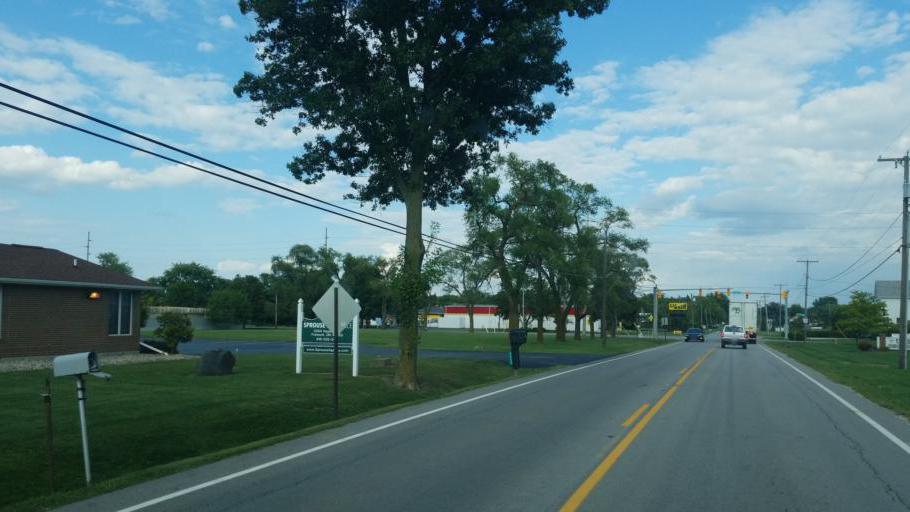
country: US
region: Ohio
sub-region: Sandusky County
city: Stony Prairie
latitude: 41.3421
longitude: -83.1476
